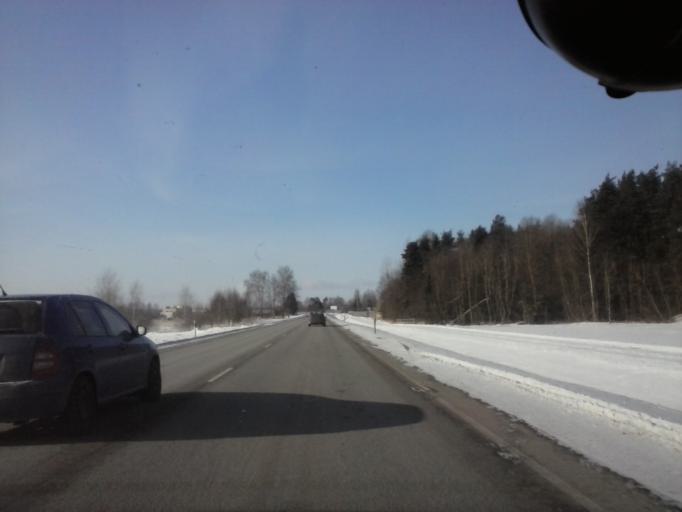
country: EE
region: Tartu
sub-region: Tartu linn
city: Tartu
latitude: 58.3585
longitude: 26.6316
